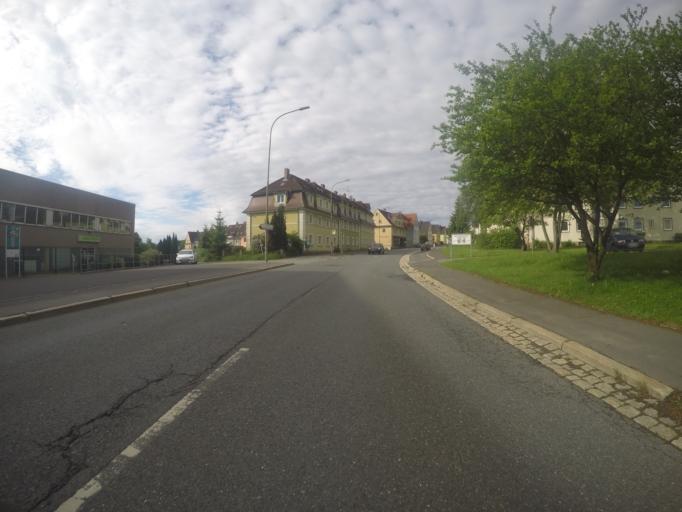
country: DE
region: Bavaria
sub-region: Upper Franconia
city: Schonwald
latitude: 50.2020
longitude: 12.0947
